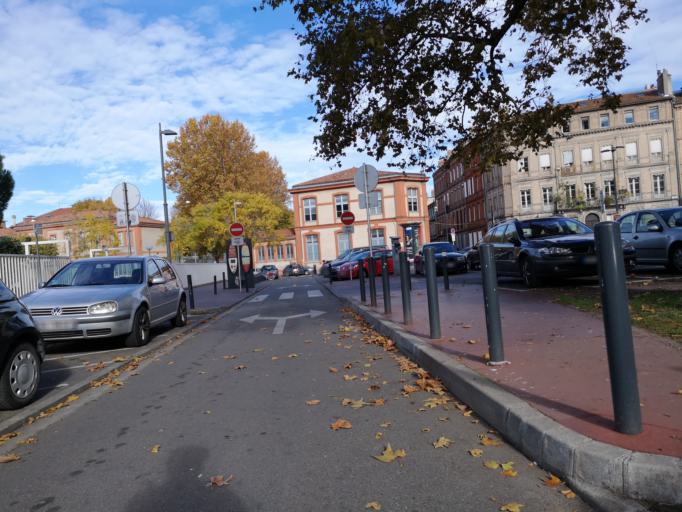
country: FR
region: Midi-Pyrenees
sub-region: Departement de la Haute-Garonne
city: Toulouse
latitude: 43.6060
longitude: 1.4382
